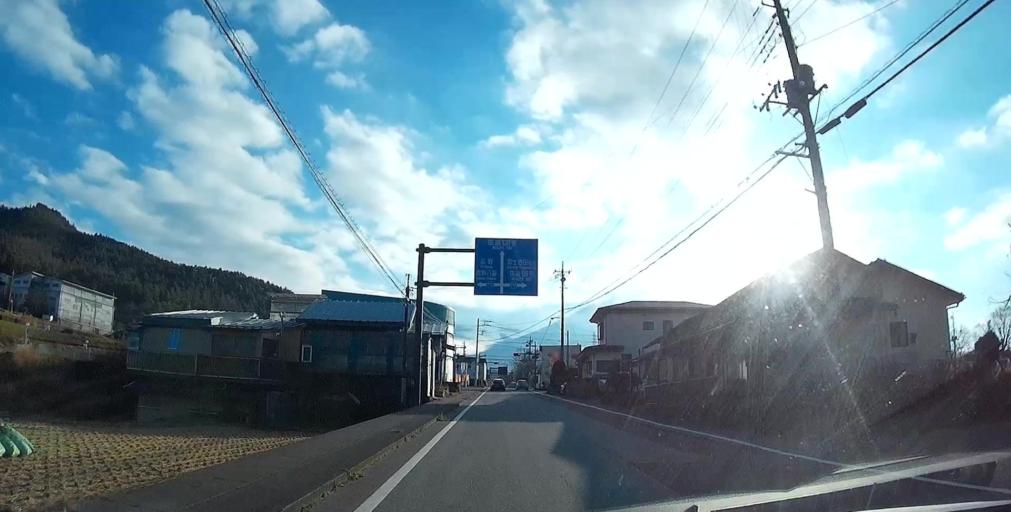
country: JP
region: Yamanashi
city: Fujikawaguchiko
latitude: 35.4787
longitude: 138.8164
